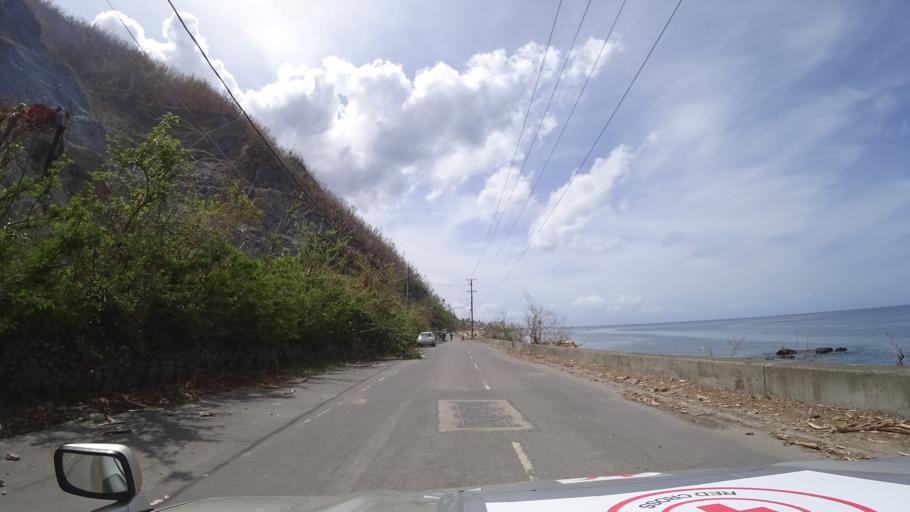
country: DM
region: Saint Luke
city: Pointe Michel
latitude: 15.2698
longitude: -61.3757
